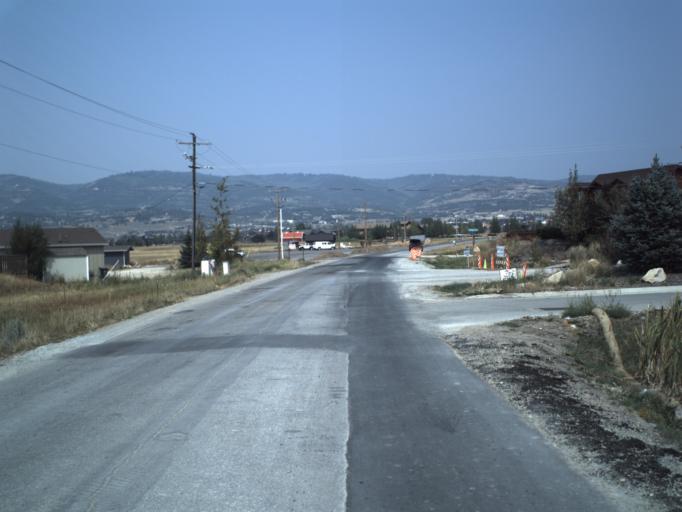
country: US
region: Utah
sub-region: Summit County
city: Snyderville
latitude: 40.7350
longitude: -111.4997
